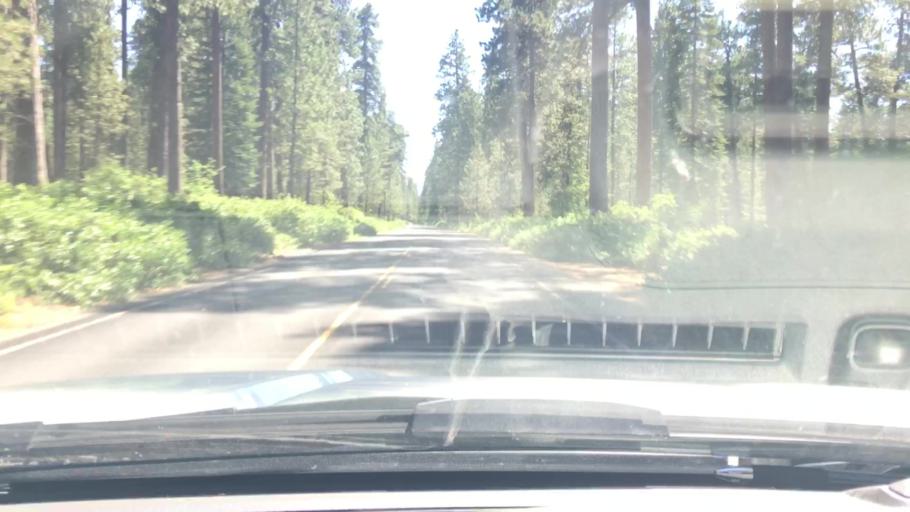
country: US
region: Oregon
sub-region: Deschutes County
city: Sisters
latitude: 44.4189
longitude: -121.6694
